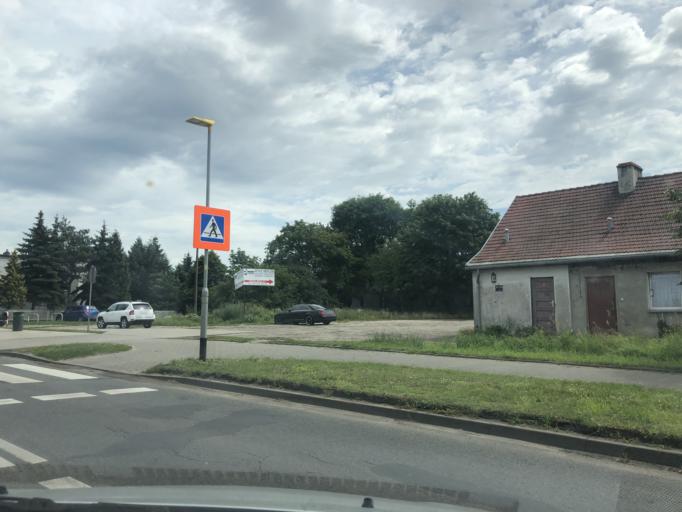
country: PL
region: Greater Poland Voivodeship
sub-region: Powiat poznanski
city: Lubon
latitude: 52.3630
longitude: 16.8916
